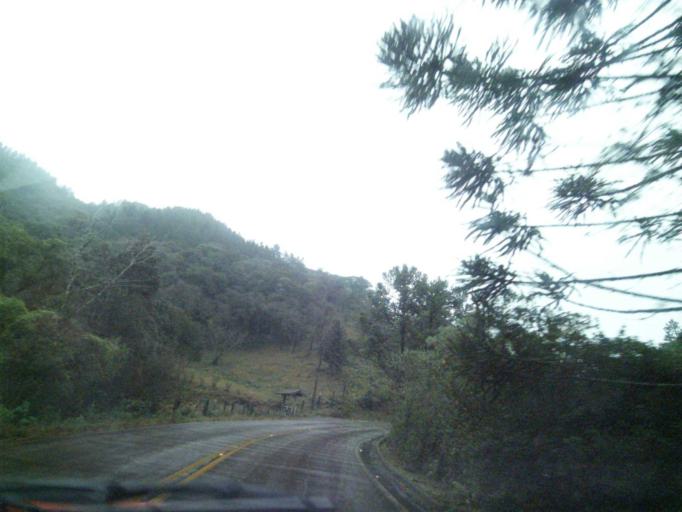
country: BR
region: Santa Catarina
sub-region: Anitapolis
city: Anitapolis
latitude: -27.8002
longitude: -49.0455
